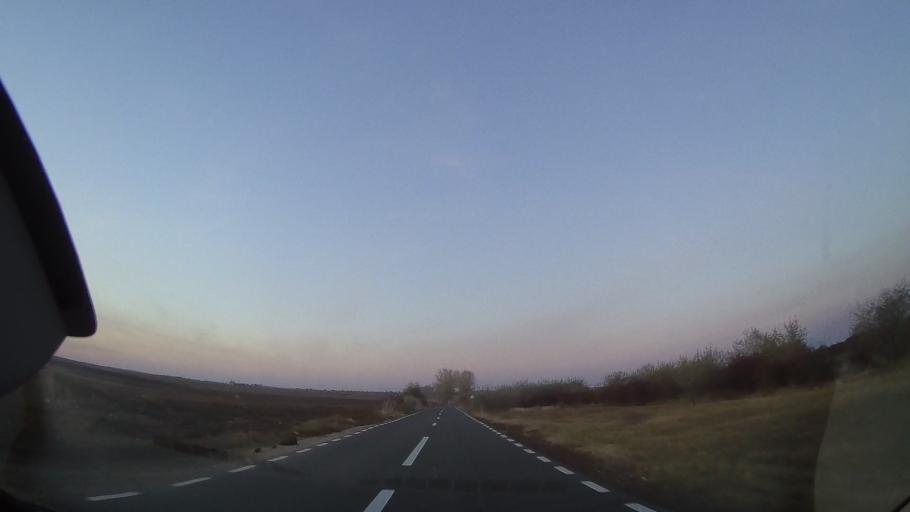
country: RO
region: Constanta
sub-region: Comuna Cobadin
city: Cobadin
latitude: 44.0362
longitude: 28.2593
